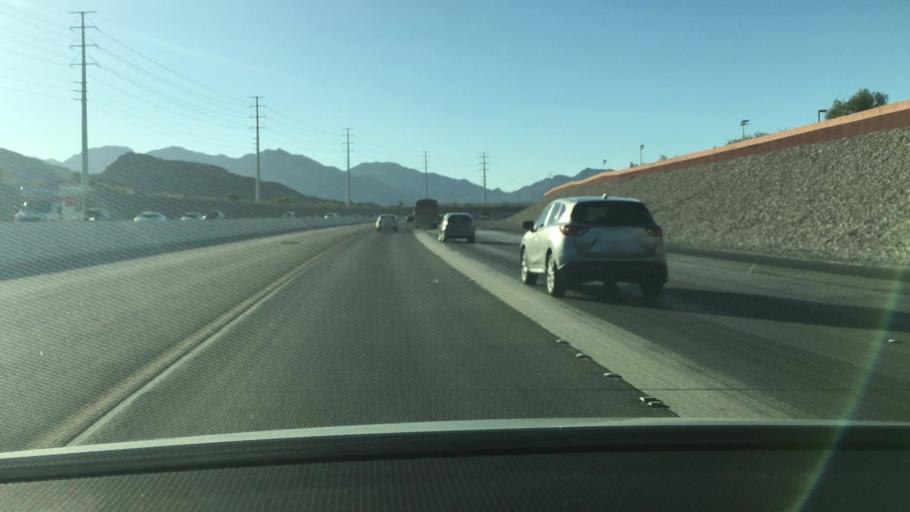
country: US
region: Nevada
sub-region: Clark County
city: Summerlin South
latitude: 36.1256
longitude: -115.3320
